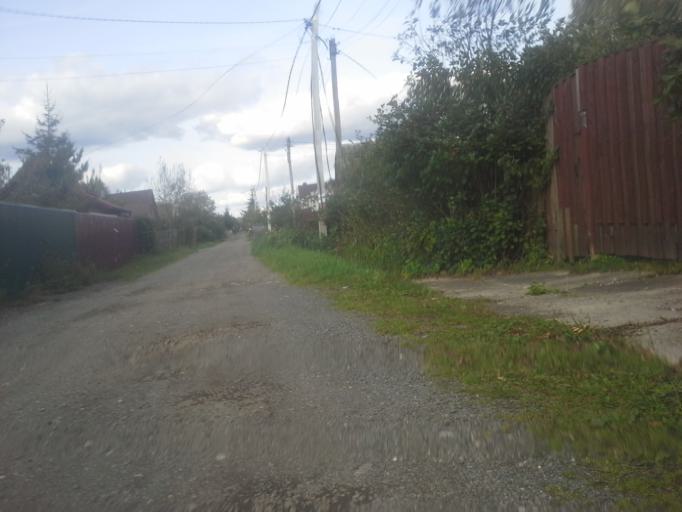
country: RU
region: Moskovskaya
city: Kievskij
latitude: 55.4262
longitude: 36.8909
